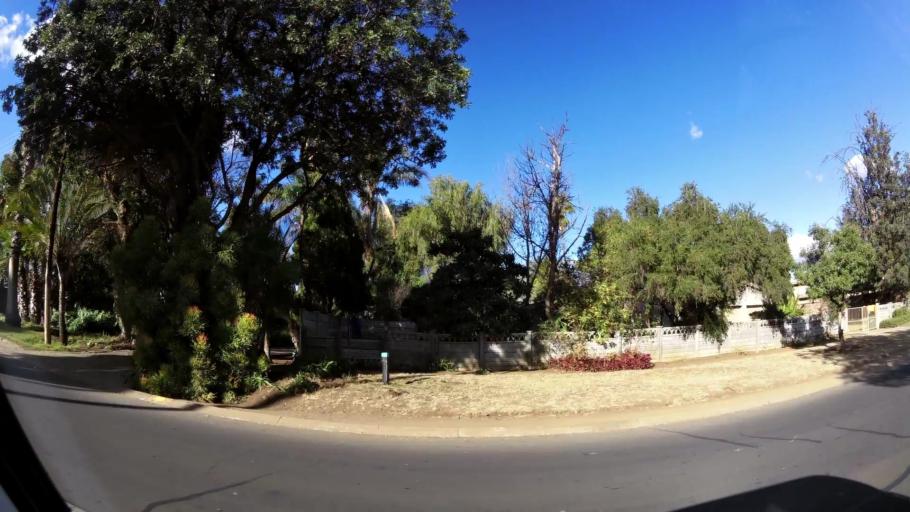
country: ZA
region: Limpopo
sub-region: Capricorn District Municipality
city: Polokwane
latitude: -23.9306
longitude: 29.4524
